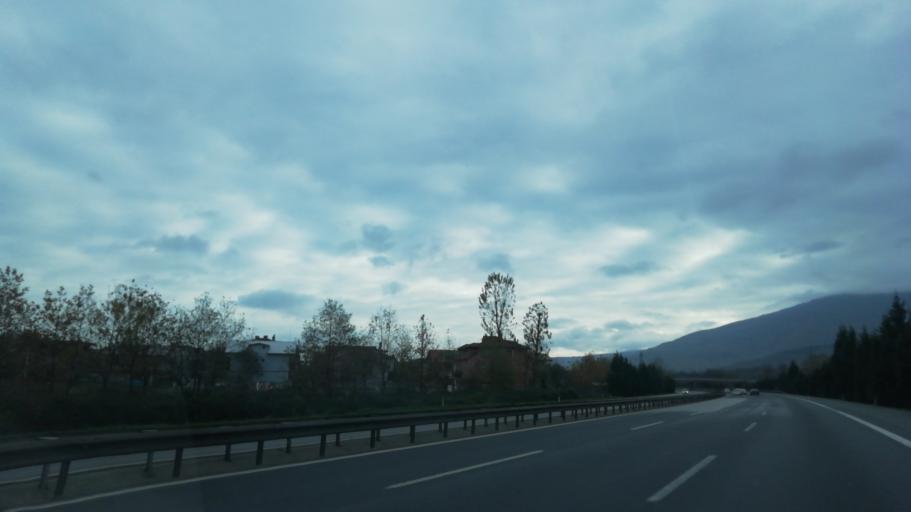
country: TR
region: Kocaeli
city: Derbent
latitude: 40.7160
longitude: 30.1132
